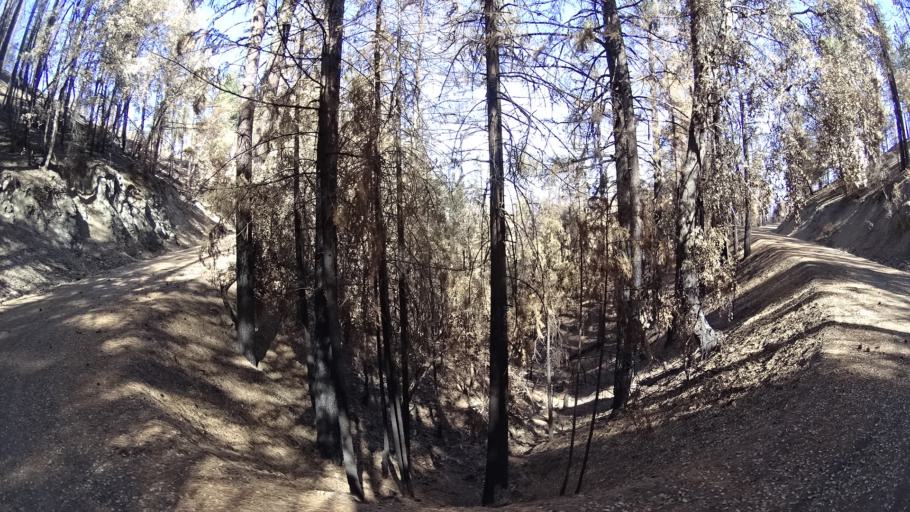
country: US
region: California
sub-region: Tehama County
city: Rancho Tehama Reserve
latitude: 39.6654
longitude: -122.7095
